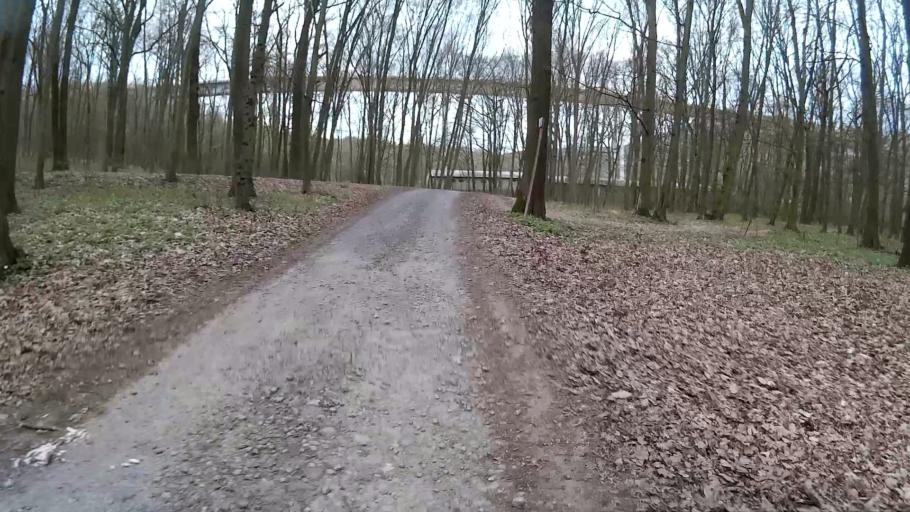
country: CZ
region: South Moravian
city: Ivancice
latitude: 49.0806
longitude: 16.4078
